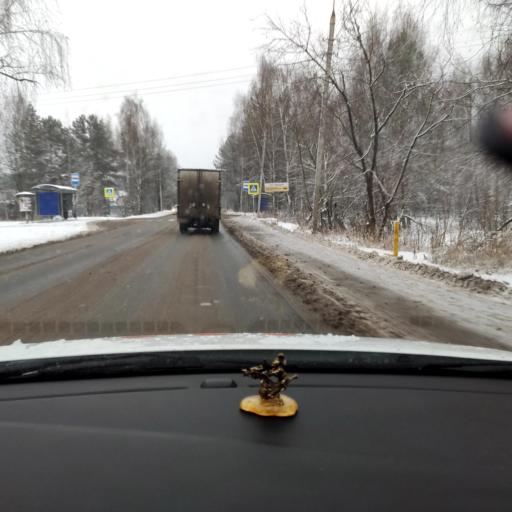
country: RU
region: Tatarstan
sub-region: Zelenodol'skiy Rayon
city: Zelenodolsk
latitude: 55.8670
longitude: 48.5395
